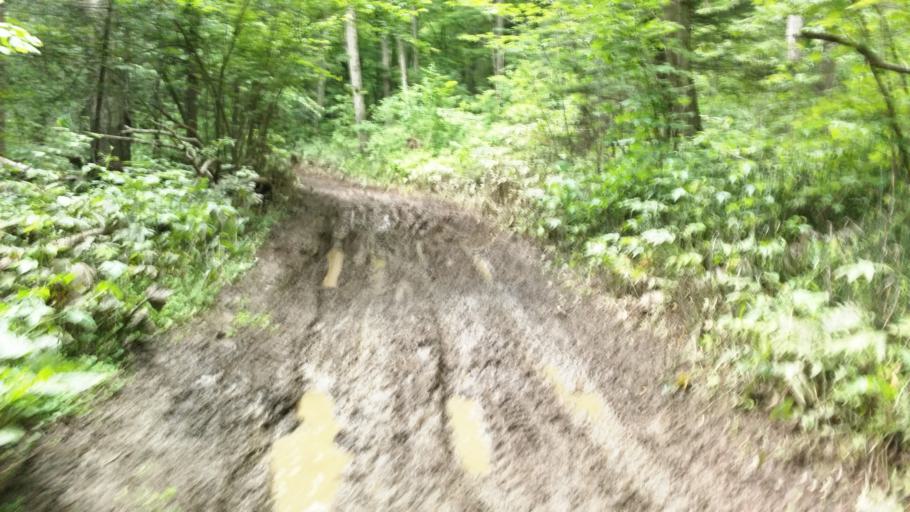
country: RU
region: Primorskiy
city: Trudovoye
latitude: 43.2071
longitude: 132.0064
